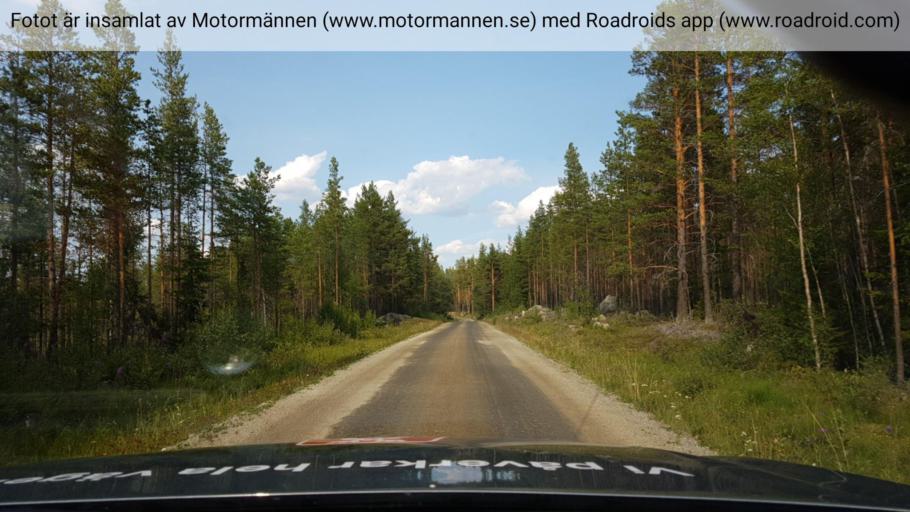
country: SE
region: Jaemtland
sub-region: Braecke Kommun
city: Braecke
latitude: 62.4826
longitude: 14.9193
